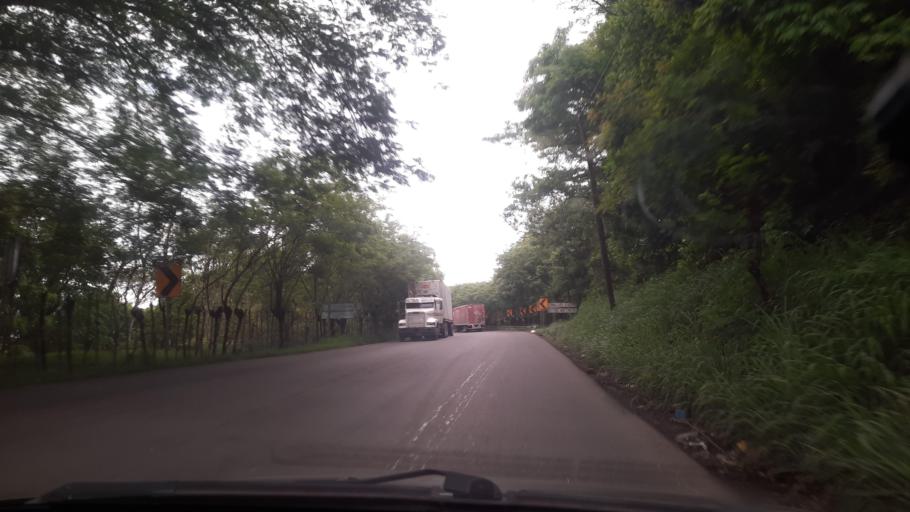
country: GT
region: Izabal
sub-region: Municipio de Los Amates
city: Los Amates
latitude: 15.2528
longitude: -89.1197
